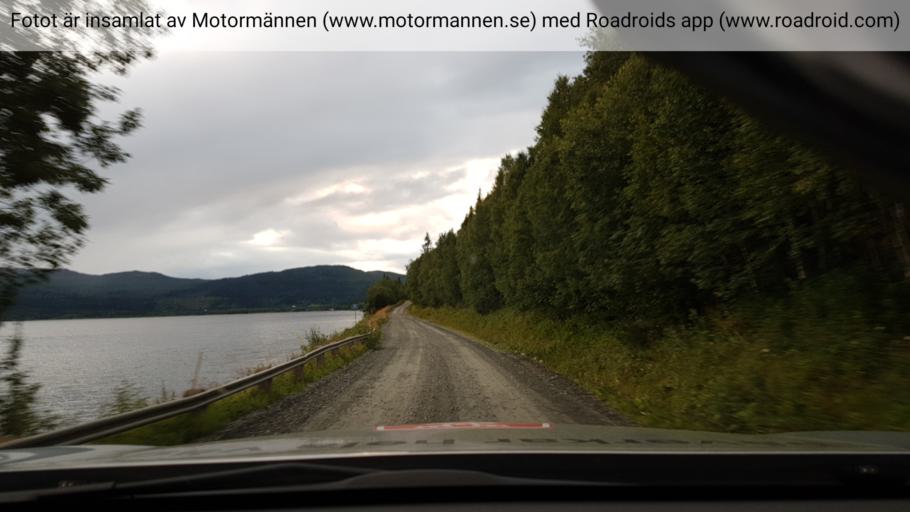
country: NO
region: Nordland
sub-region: Hattfjelldal
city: Hattfjelldal
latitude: 65.6463
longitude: 15.1883
